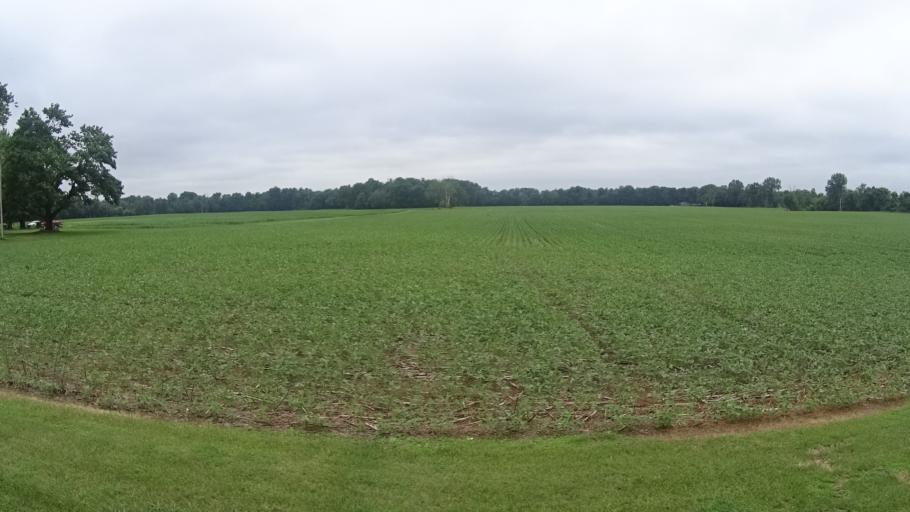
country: US
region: Ohio
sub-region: Erie County
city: Huron
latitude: 41.3450
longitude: -82.5440
